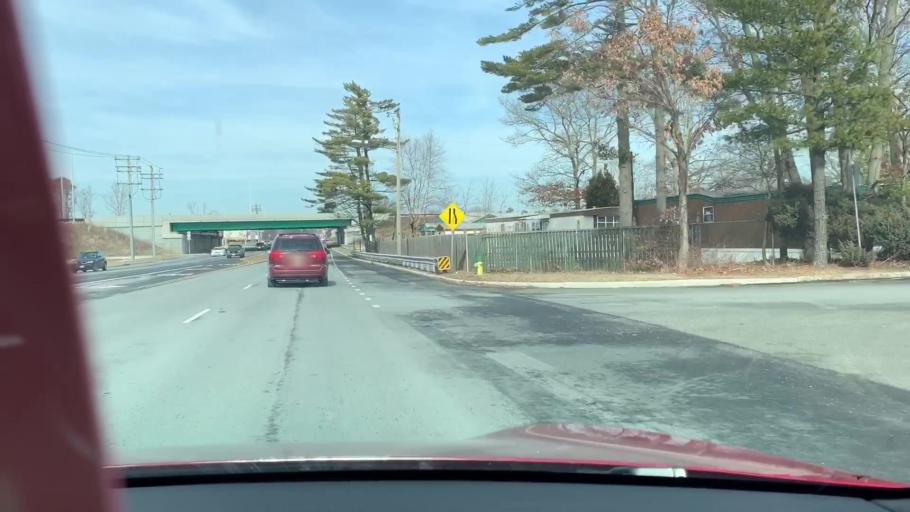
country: US
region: New Jersey
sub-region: Atlantic County
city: Northfield
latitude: 39.3968
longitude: -74.5603
